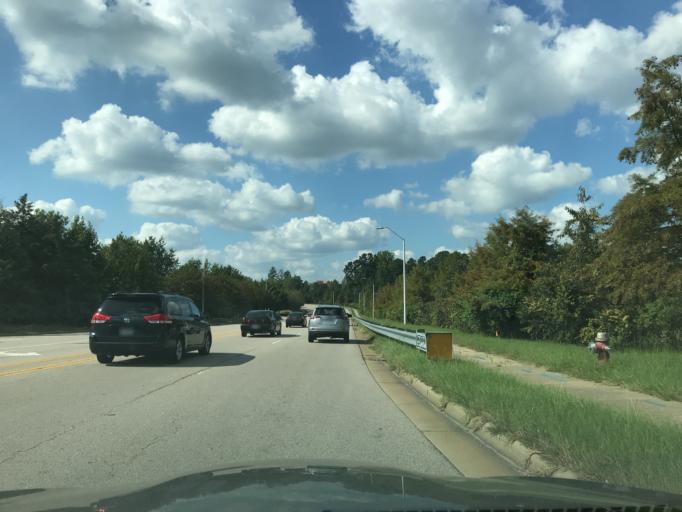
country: US
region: North Carolina
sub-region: Wake County
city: Raleigh
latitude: 35.8678
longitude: -78.5721
